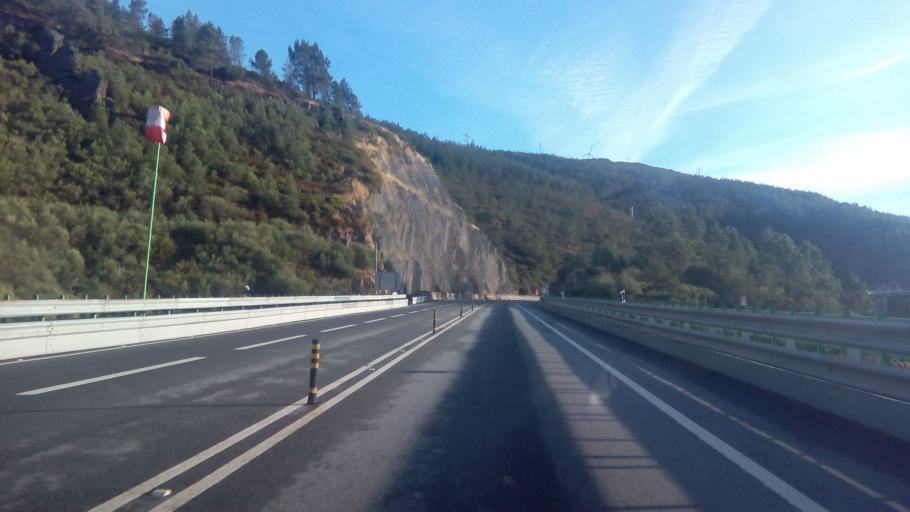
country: PT
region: Vila Real
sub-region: Mesao Frio
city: Mesao Frio
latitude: 41.2742
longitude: -7.9369
